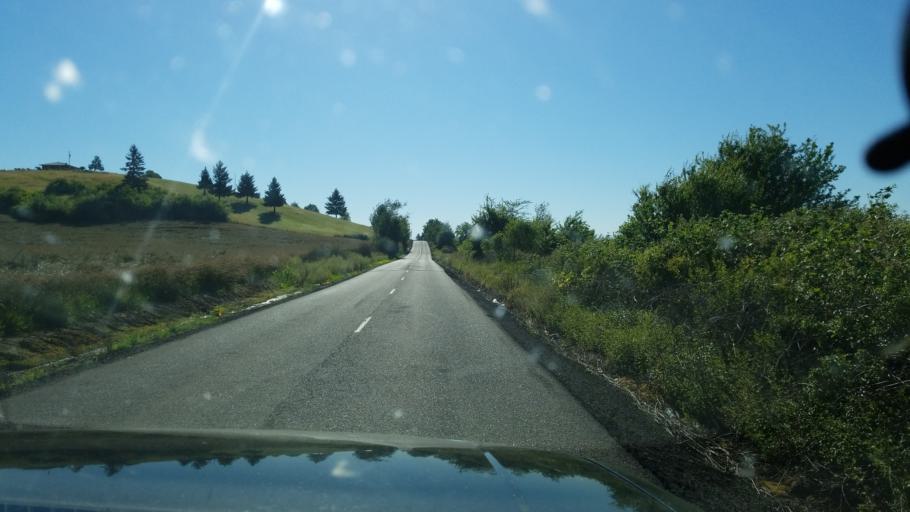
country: US
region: Oregon
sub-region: Yamhill County
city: McMinnville
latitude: 45.2451
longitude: -123.2280
